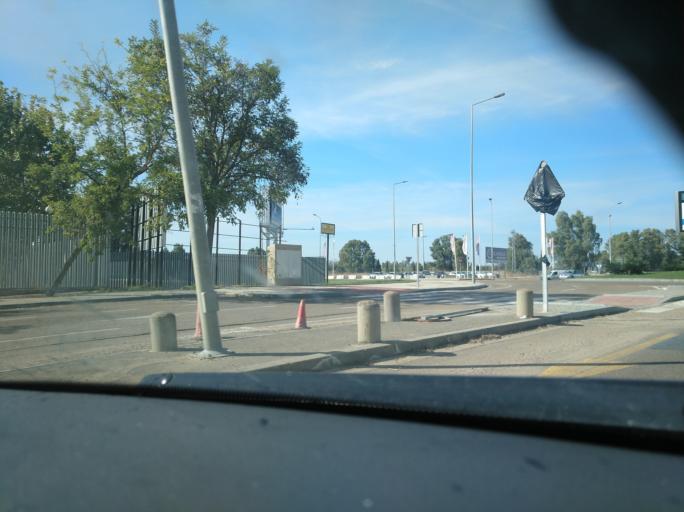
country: ES
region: Extremadura
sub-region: Provincia de Badajoz
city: Badajoz
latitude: 38.8826
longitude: -7.0248
